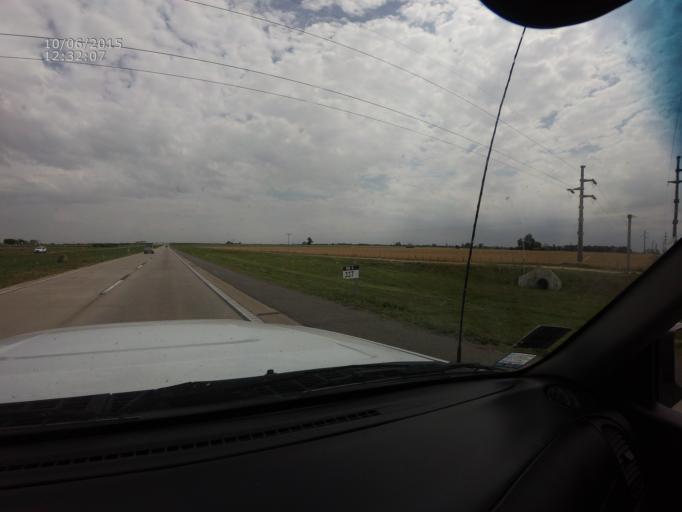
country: AR
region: Santa Fe
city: Carcarana
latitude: -32.8818
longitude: -61.1386
